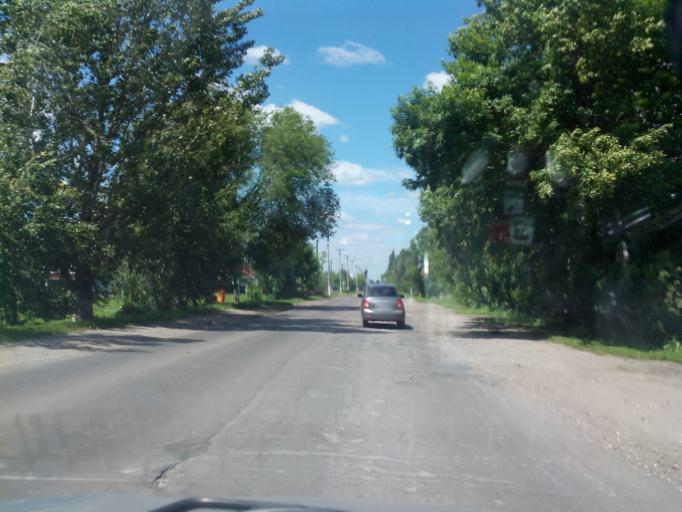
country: RU
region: Tambov
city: Zherdevka
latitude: 51.8220
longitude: 41.5029
